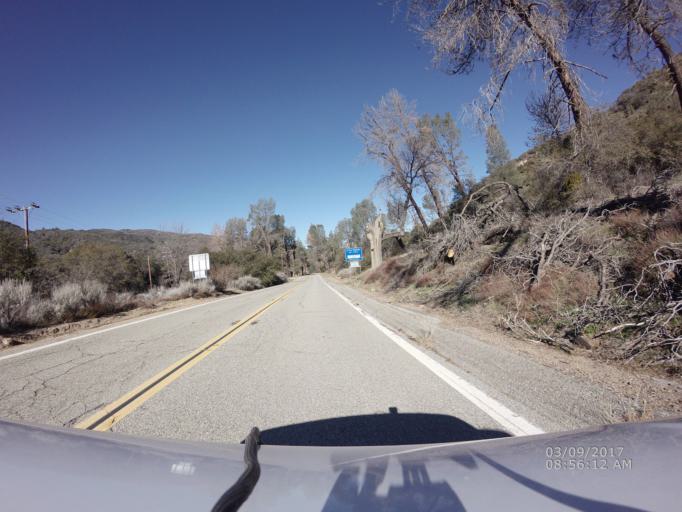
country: US
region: California
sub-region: Los Angeles County
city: Green Valley
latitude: 34.7172
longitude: -118.5750
